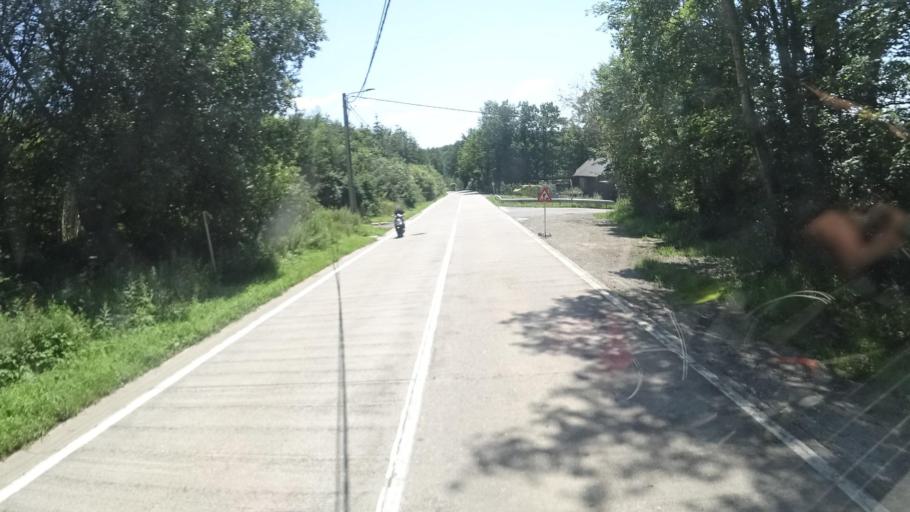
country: BE
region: Wallonia
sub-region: Province de Namur
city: Profondeville
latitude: 50.3800
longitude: 4.8133
